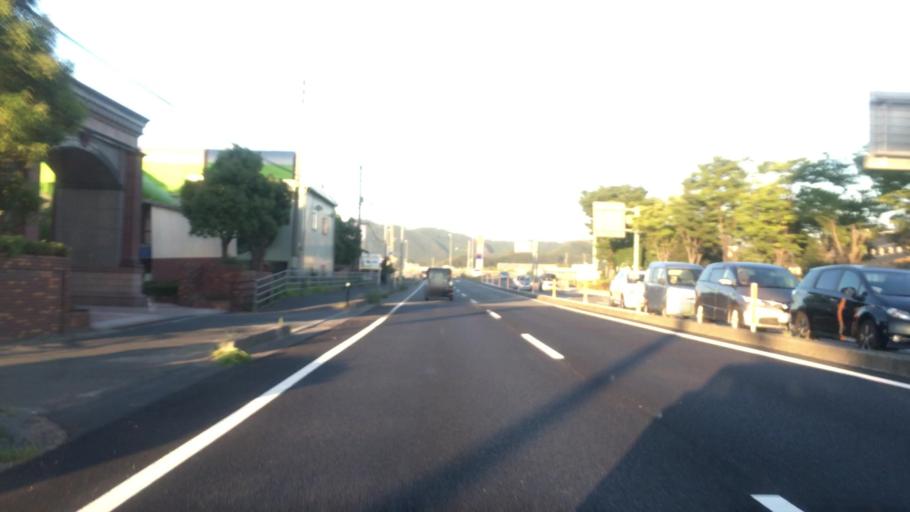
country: JP
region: Tottori
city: Tottori
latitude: 35.5194
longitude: 134.2048
